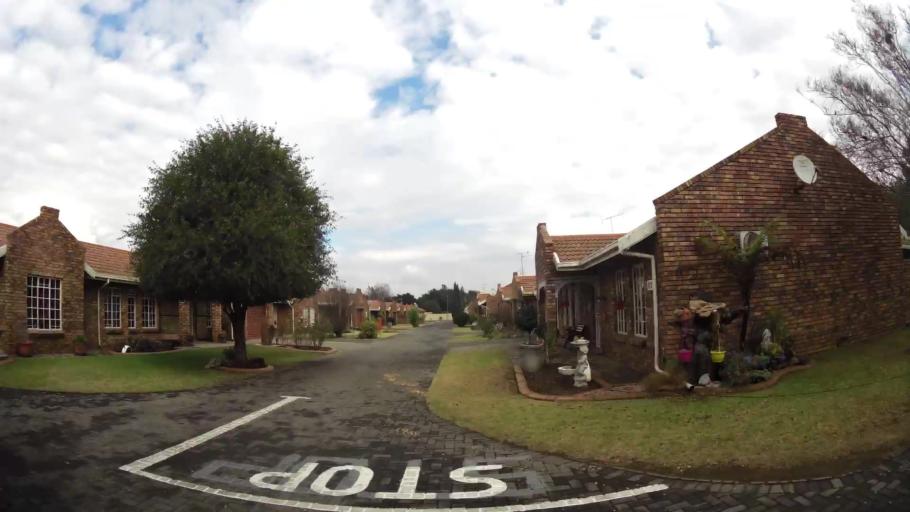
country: ZA
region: Gauteng
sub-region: Sedibeng District Municipality
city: Vereeniging
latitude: -26.6488
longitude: 27.9764
